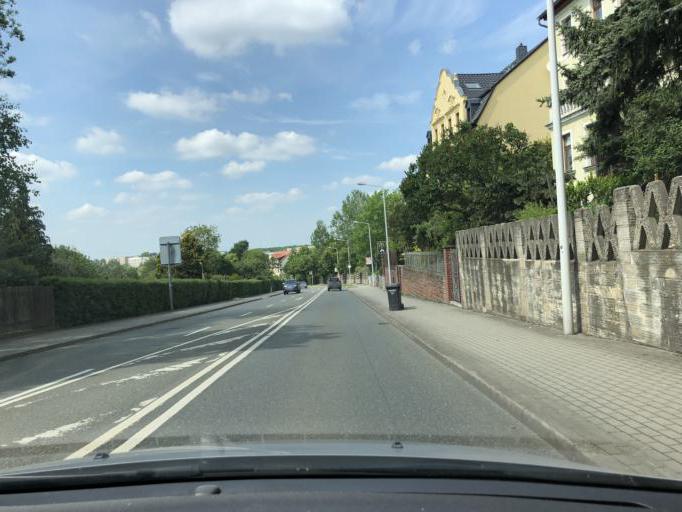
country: DE
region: Thuringia
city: Altenburg
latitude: 50.9887
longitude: 12.4267
